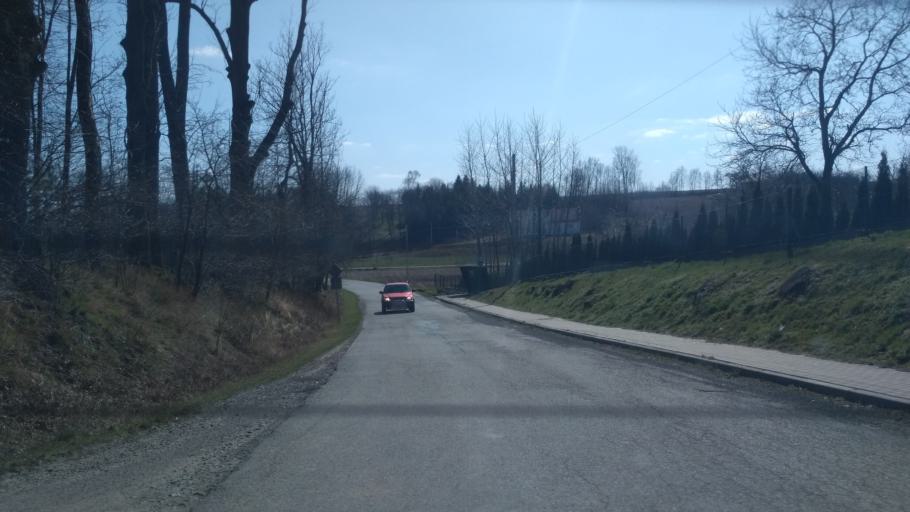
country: PL
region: Subcarpathian Voivodeship
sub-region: Powiat jaroslawski
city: Jodlowka
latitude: 49.9285
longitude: 22.4634
